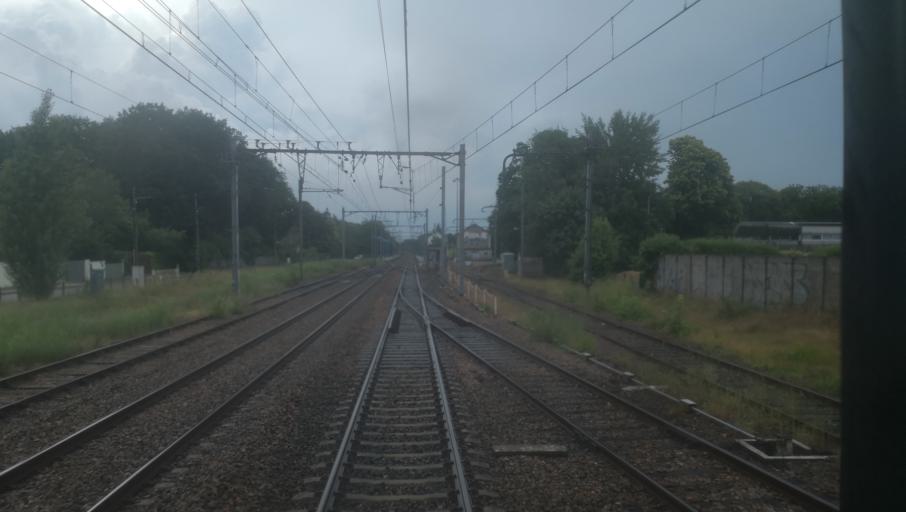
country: FR
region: Centre
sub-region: Departement du Loiret
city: Saint-Cyr-en-Val
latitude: 47.8164
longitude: 1.9470
